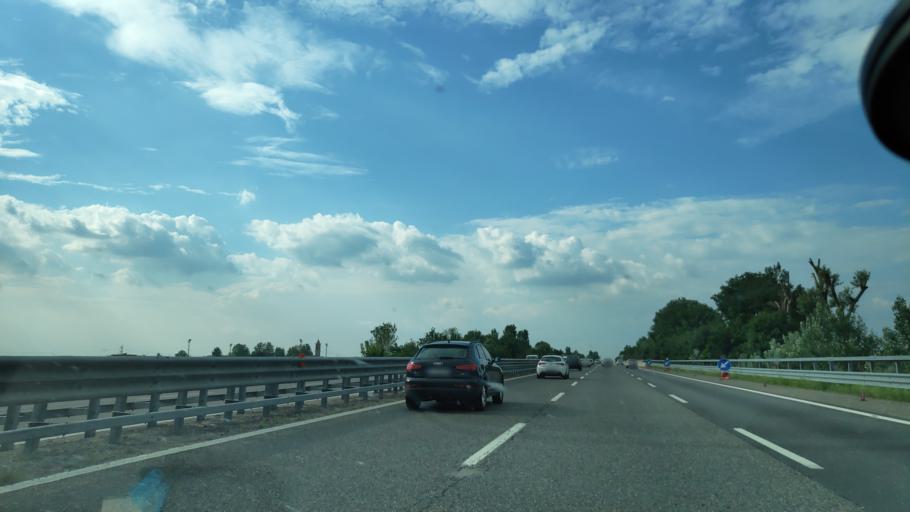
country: IT
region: Lombardy
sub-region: Provincia di Pavia
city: Zerbolo
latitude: 45.2022
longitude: 9.0181
